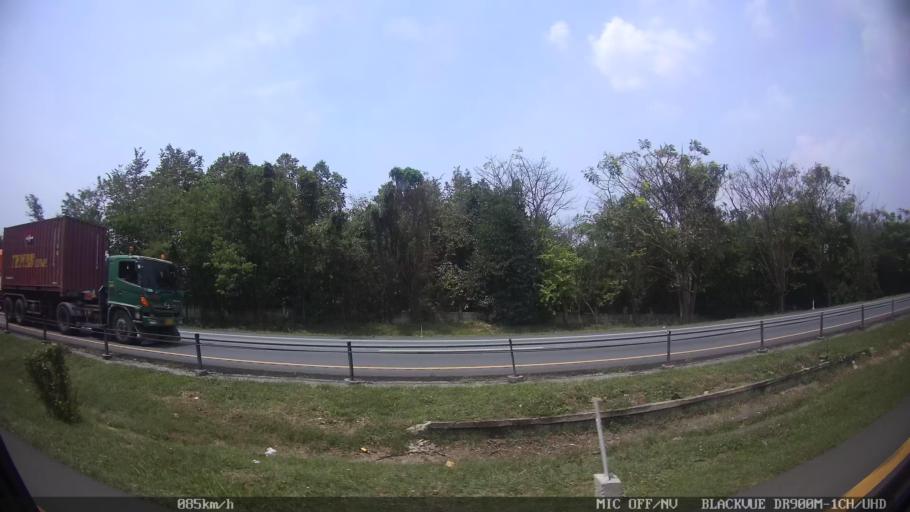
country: ID
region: Banten
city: Serang
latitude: -6.0756
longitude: 106.1307
